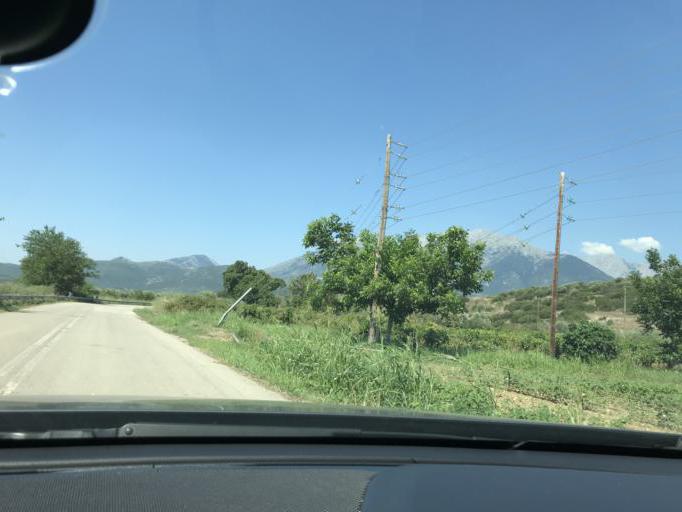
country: GR
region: Central Greece
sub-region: Nomos Fthiotidos
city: Elateia
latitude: 38.5261
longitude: 22.7953
